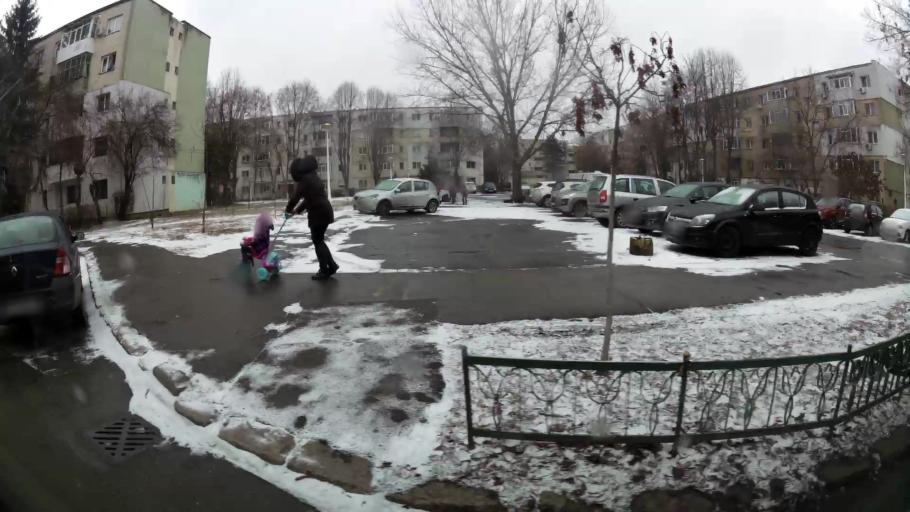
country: RO
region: Prahova
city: Ploiesti
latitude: 44.9613
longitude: 26.0068
